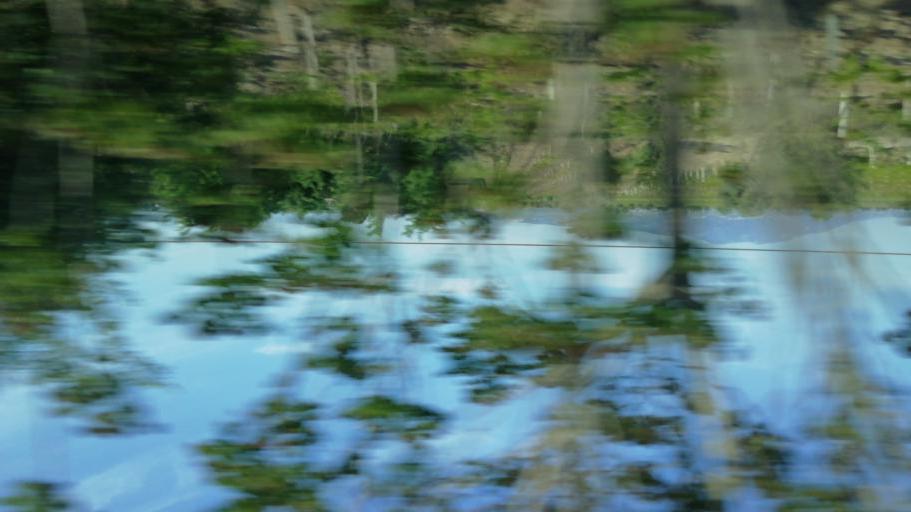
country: TR
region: Manisa
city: Saruhanli
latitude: 38.7344
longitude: 27.5899
